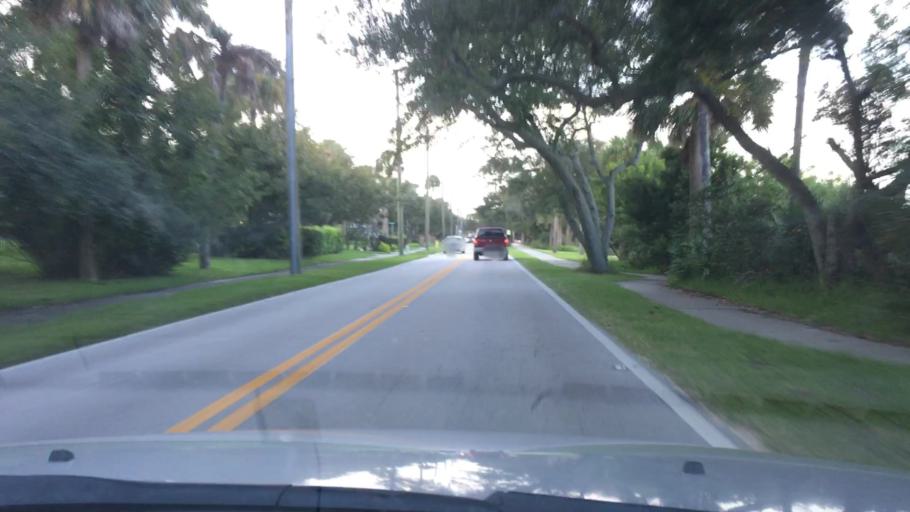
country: US
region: Florida
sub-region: Volusia County
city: Ormond Beach
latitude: 29.2817
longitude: -81.0537
